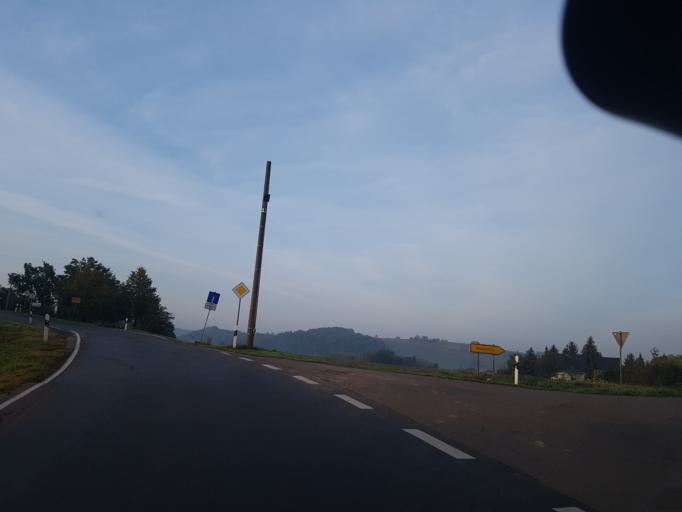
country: DE
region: Saxony
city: Grossweitzschen
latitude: 51.1194
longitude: 13.0499
